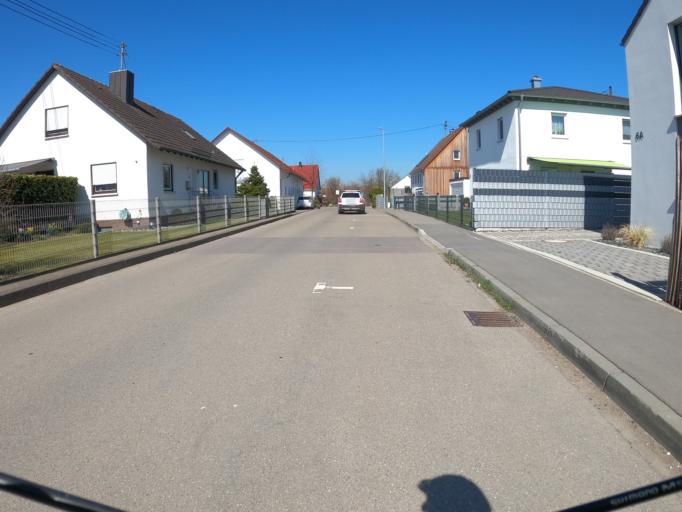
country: DE
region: Bavaria
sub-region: Swabia
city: Nersingen
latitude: 48.4299
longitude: 10.1268
